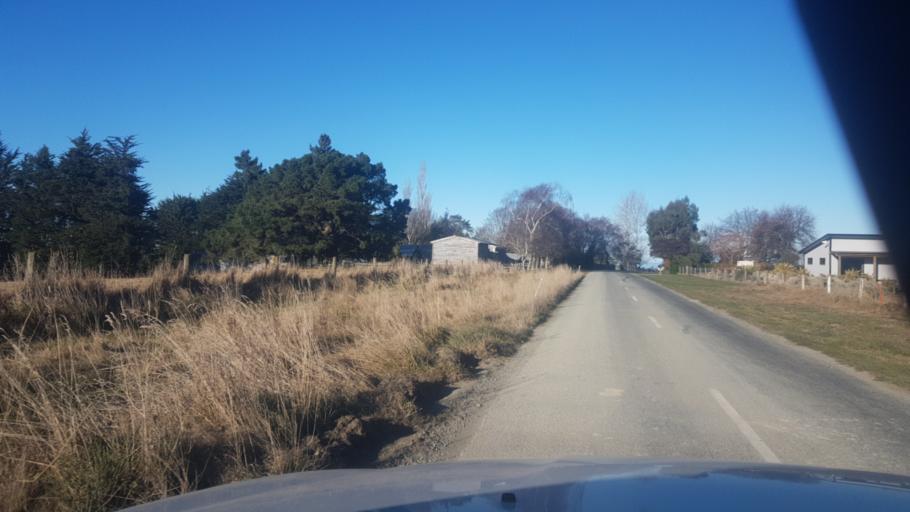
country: NZ
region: Canterbury
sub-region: Timaru District
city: Pleasant Point
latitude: -44.3720
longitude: 171.0766
